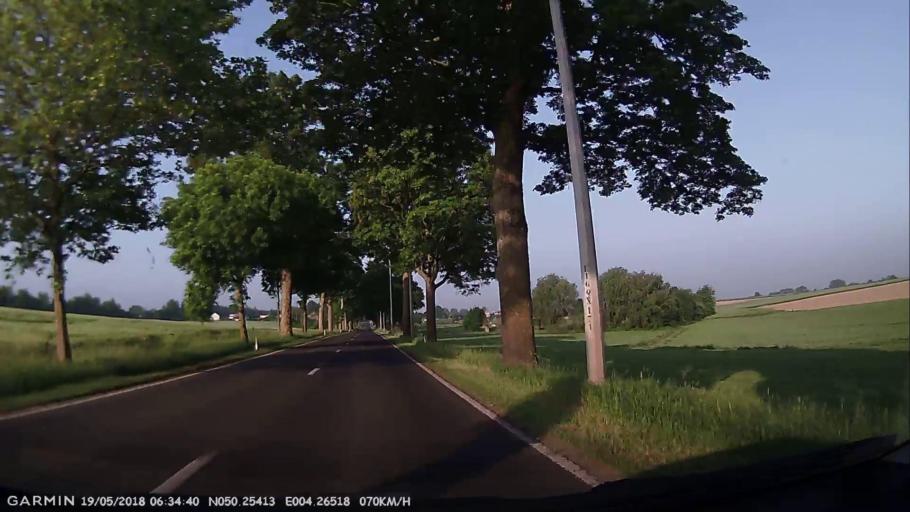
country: BE
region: Wallonia
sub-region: Province du Hainaut
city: Beaumont
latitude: 50.2540
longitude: 4.2650
